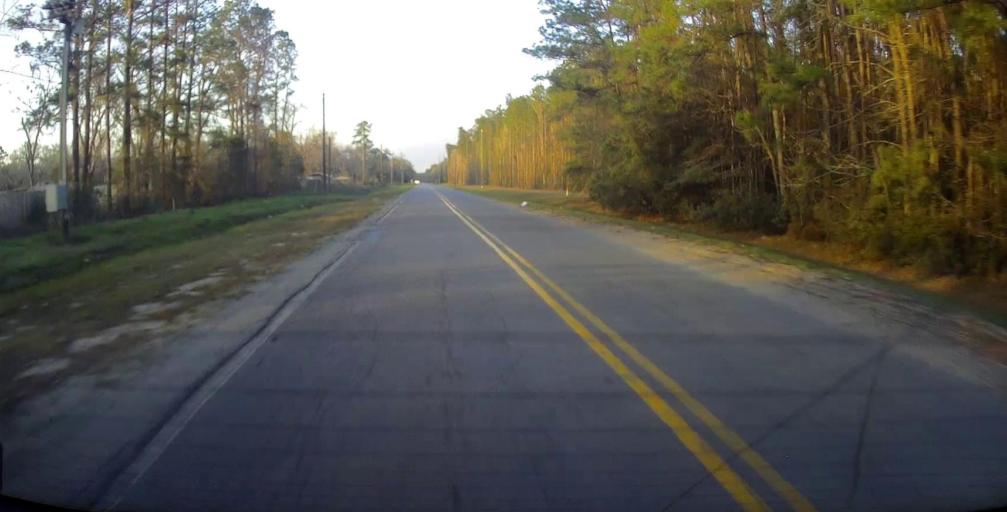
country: US
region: Georgia
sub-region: Chatham County
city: Bloomingdale
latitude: 32.1478
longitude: -81.3897
